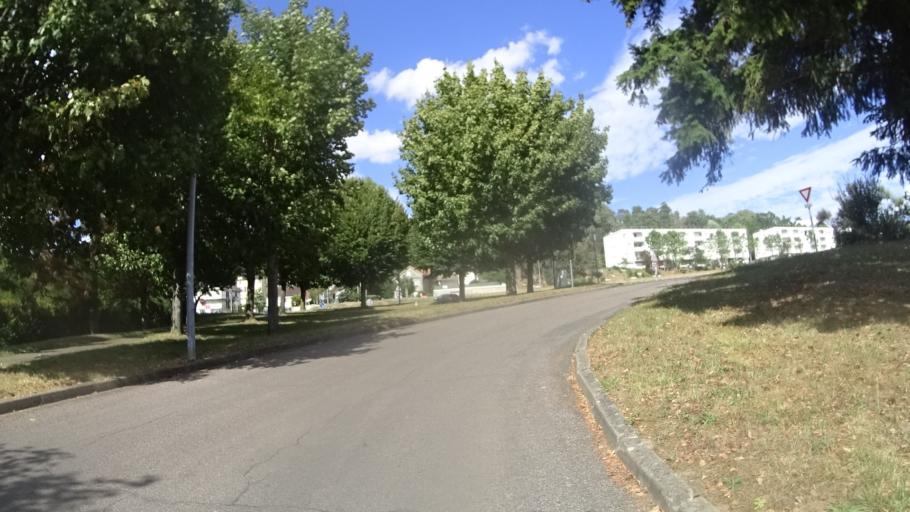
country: FR
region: Ile-de-France
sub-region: Departement de l'Essonne
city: La Ferte-Alais
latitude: 48.4764
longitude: 2.3548
